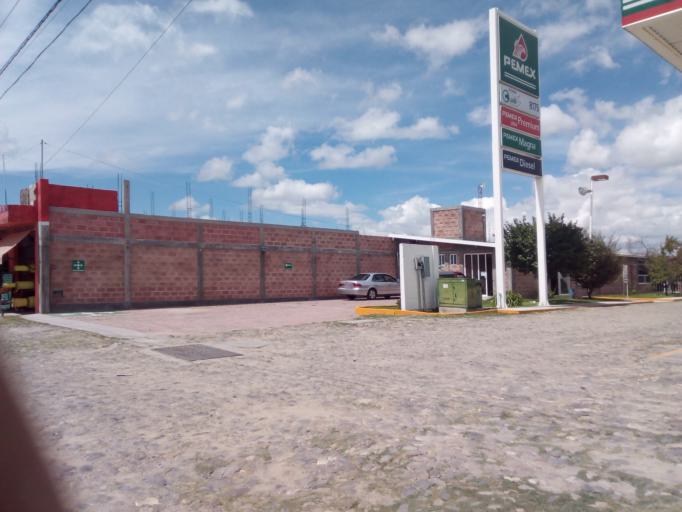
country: MX
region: Guanajuato
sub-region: San Jose Iturbide
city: Prados del Rosario
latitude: 21.0128
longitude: -100.3897
